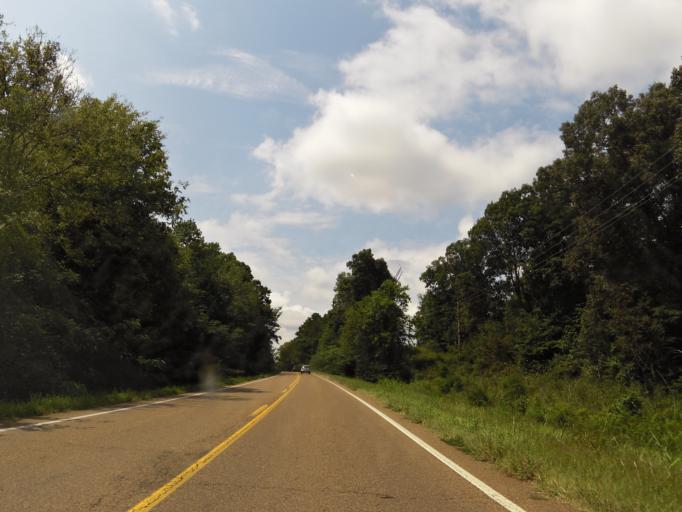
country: US
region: Tennessee
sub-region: Decatur County
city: Decaturville
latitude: 35.5422
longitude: -88.2081
